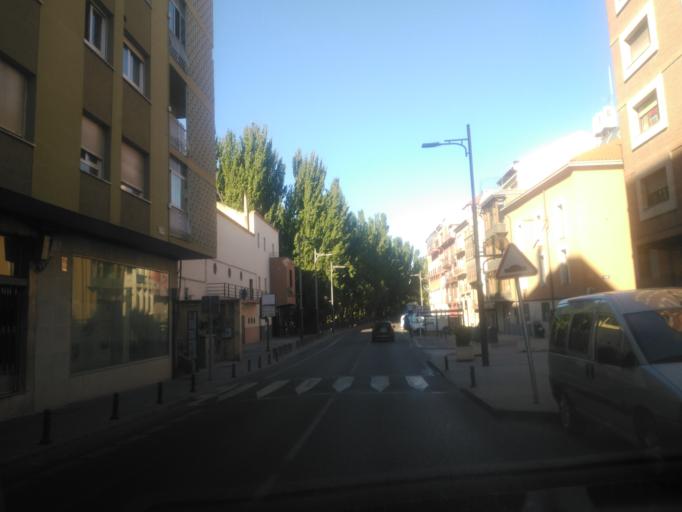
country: ES
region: Castille and Leon
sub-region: Provincia de Burgos
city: Aranda de Duero
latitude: 41.6699
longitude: -3.6878
